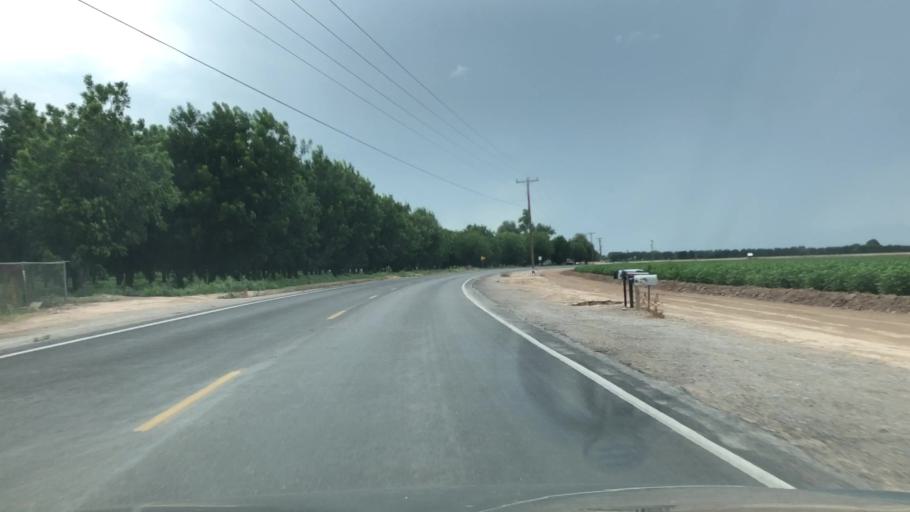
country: US
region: New Mexico
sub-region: Dona Ana County
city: La Union
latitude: 31.9708
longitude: -106.6518
